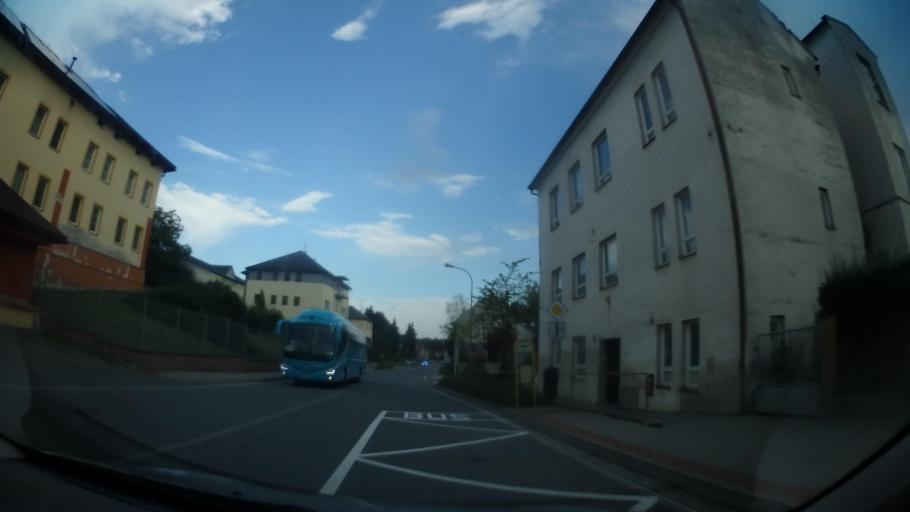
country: CZ
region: Olomoucky
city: Zabreh
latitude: 49.8866
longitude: 16.8656
